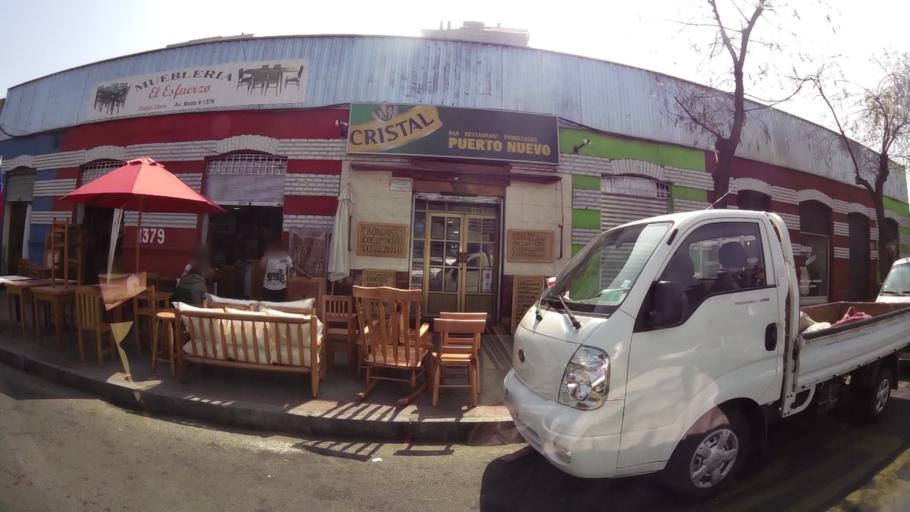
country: CL
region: Santiago Metropolitan
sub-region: Provincia de Santiago
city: Santiago
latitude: -33.4599
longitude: -70.6528
